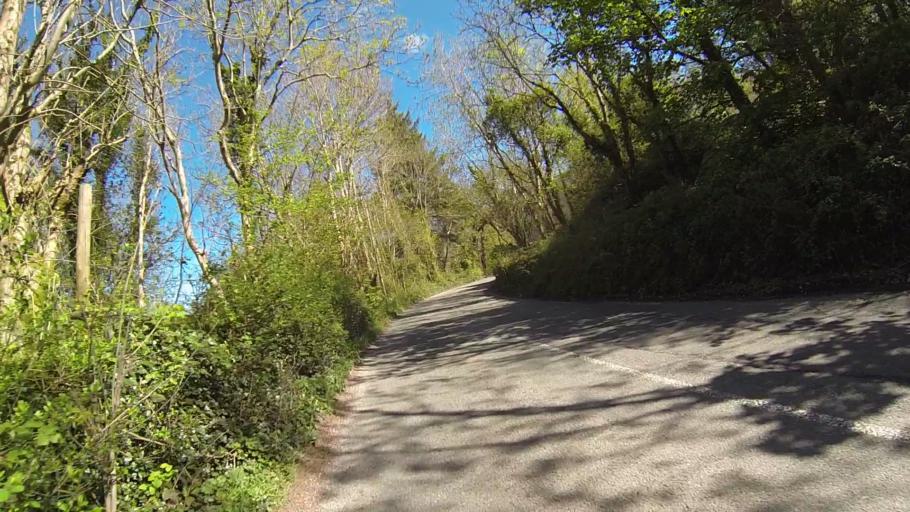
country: IE
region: Munster
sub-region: Ciarrai
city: Kenmare
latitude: 51.8542
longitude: -9.6271
